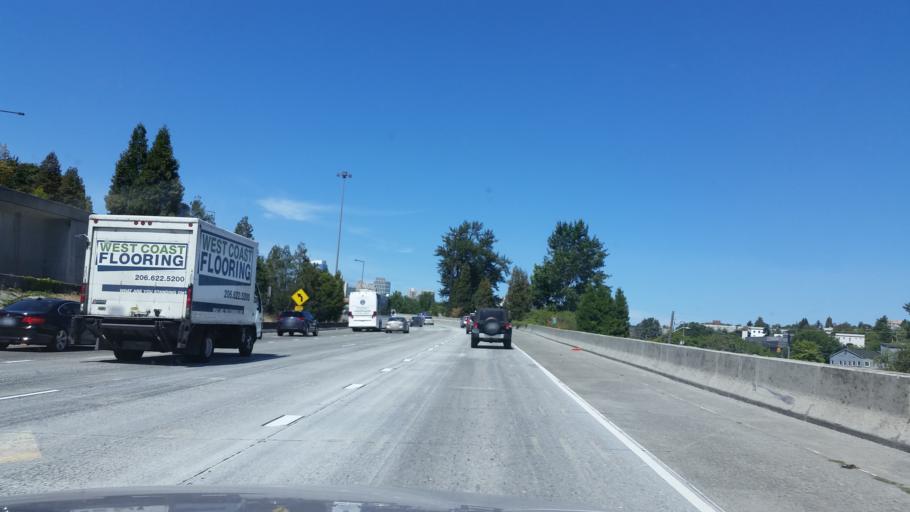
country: US
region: Washington
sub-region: King County
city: Seattle
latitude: 47.5932
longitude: -122.3118
